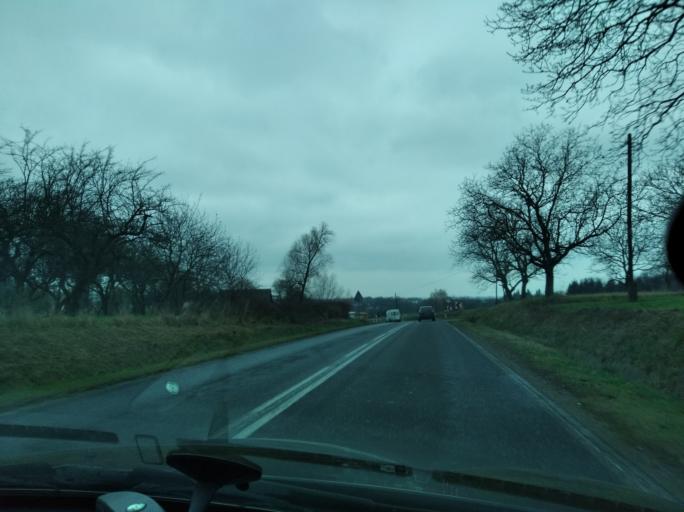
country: PL
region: Subcarpathian Voivodeship
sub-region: Powiat przeworski
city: Sietesz
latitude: 49.9990
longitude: 22.3610
